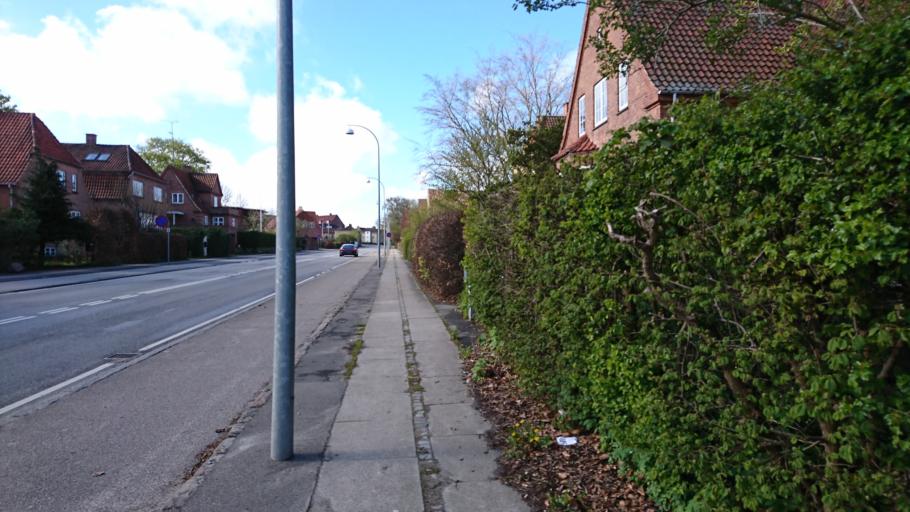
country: DK
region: Zealand
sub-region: Roskilde Kommune
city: Roskilde
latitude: 55.6432
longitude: 12.0736
